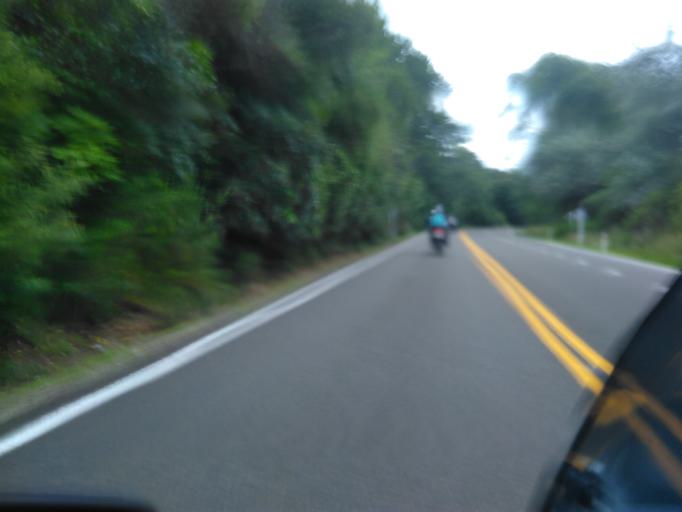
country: NZ
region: Bay of Plenty
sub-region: Opotiki District
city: Opotiki
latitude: -38.3950
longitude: 177.5614
